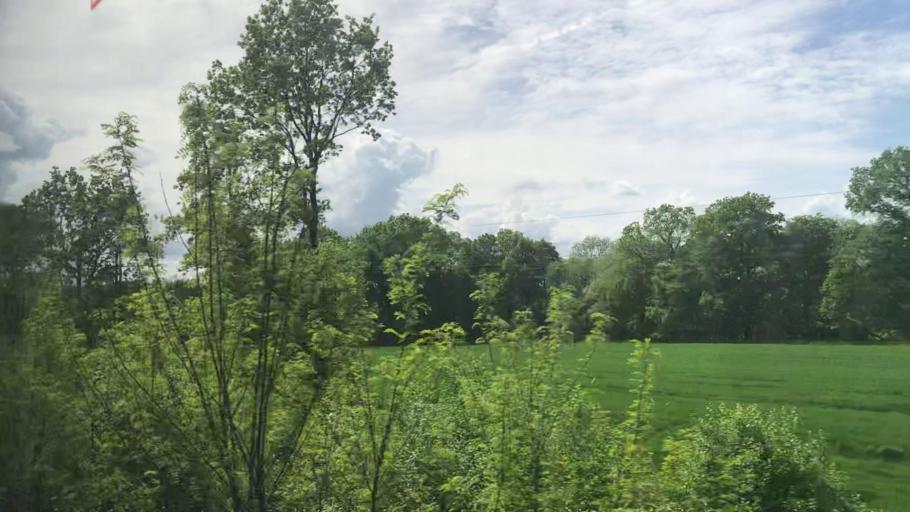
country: PL
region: Lower Silesian Voivodeship
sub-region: Powiat swidnicki
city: Jaworzyna Slaska
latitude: 50.8923
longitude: 16.3982
